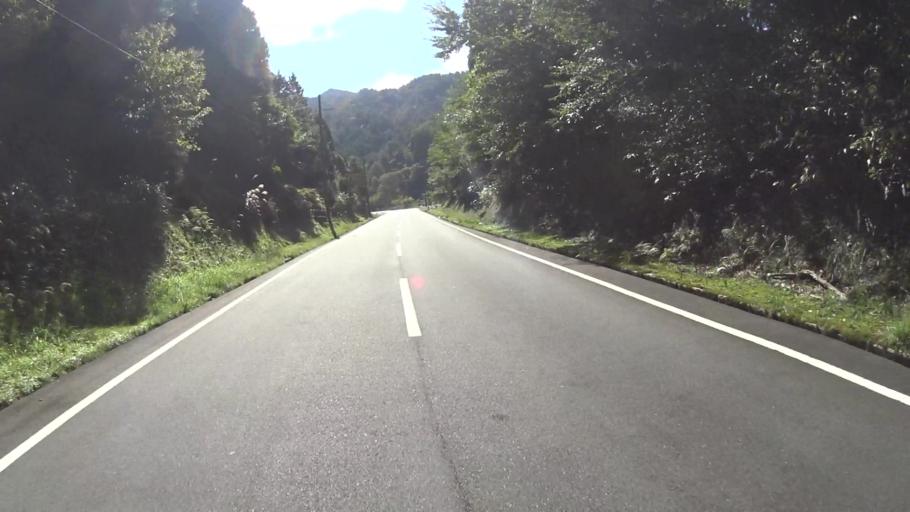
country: JP
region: Hyogo
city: Toyooka
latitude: 35.5358
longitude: 134.9789
